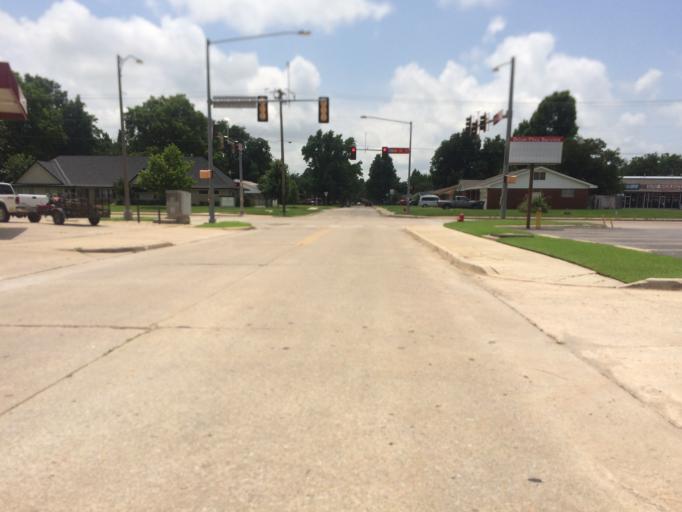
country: US
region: Oklahoma
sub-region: Cleveland County
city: Norman
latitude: 35.2189
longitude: -97.4683
